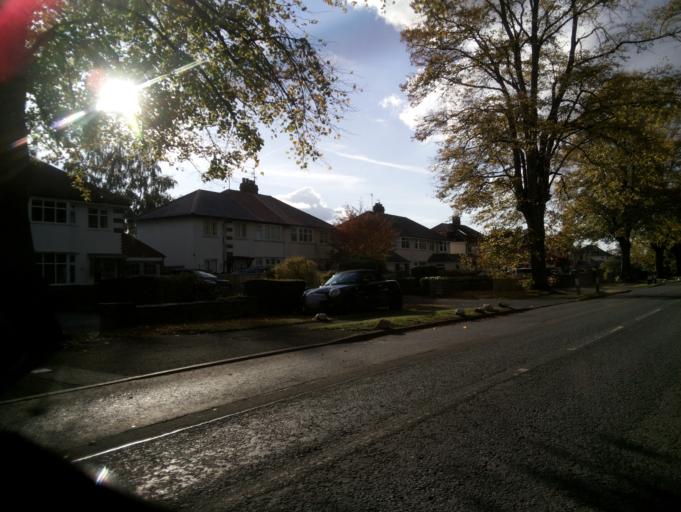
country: GB
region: England
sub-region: Herefordshire
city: Belmont
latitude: 52.0665
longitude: -2.7583
